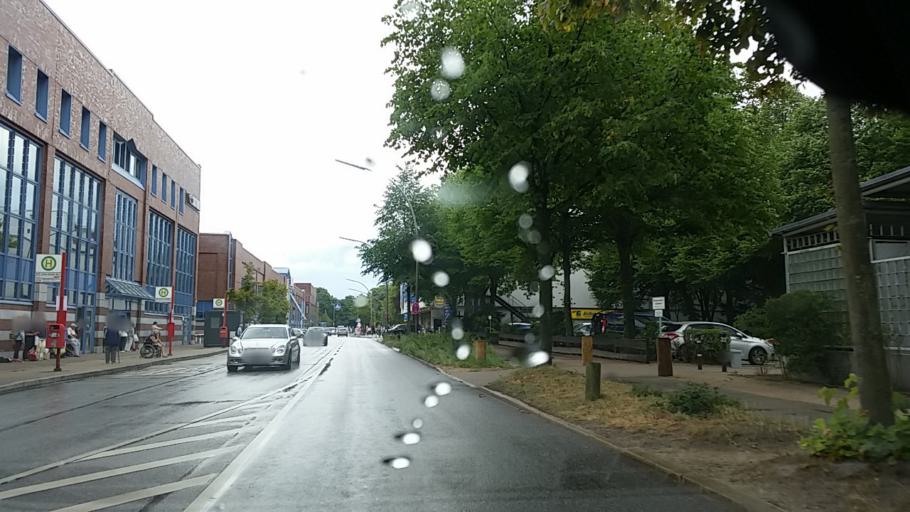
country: DE
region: Hamburg
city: Eidelstedt
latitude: 53.5700
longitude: 9.8601
